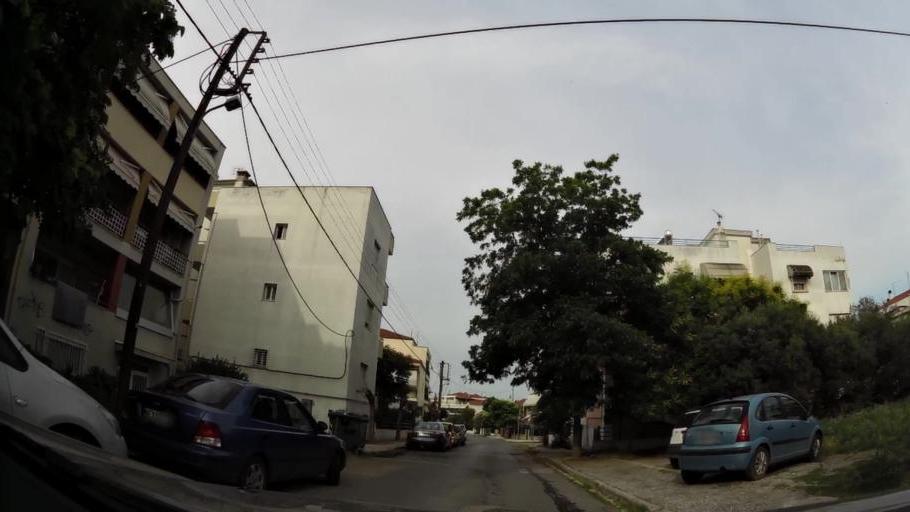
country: GR
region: Central Macedonia
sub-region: Nomos Thessalonikis
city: Thermi
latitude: 40.5490
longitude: 23.0192
